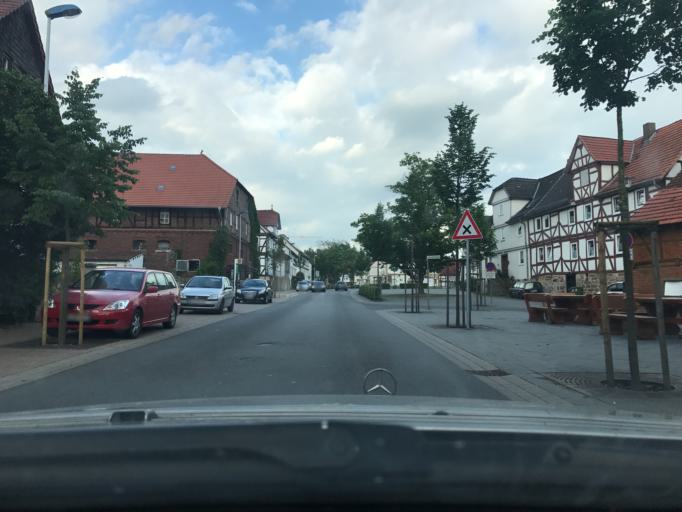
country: DE
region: Hesse
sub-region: Regierungsbezirk Kassel
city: Guxhagen
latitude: 51.2280
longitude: 9.4942
